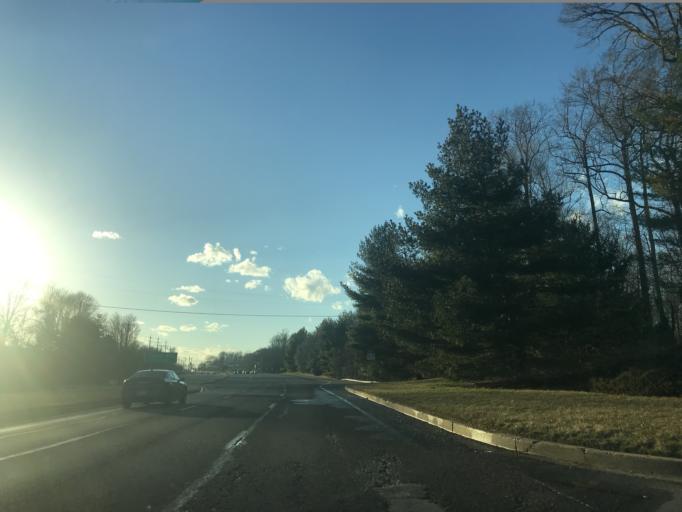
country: US
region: Maryland
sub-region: Prince George's County
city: Largo
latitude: 38.8987
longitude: -76.8181
